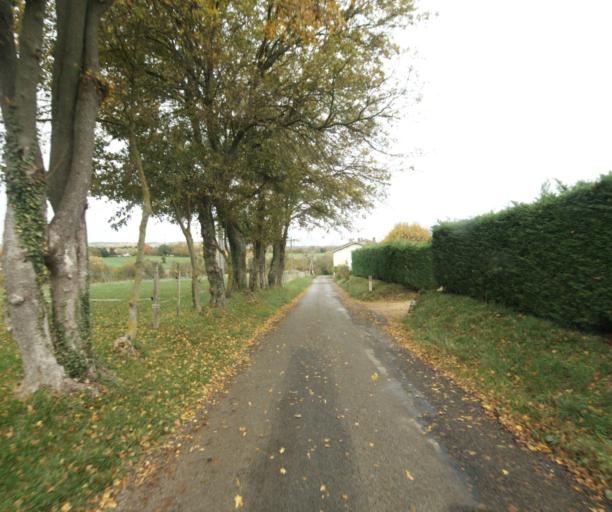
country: FR
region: Rhone-Alpes
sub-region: Departement de l'Ain
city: Pont-de-Vaux
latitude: 46.4723
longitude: 4.8743
